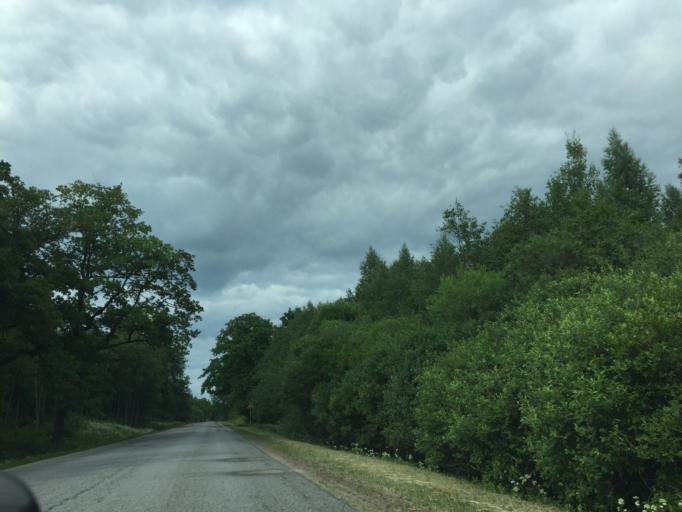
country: LV
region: Skriveri
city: Skriveri
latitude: 56.8282
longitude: 25.1263
